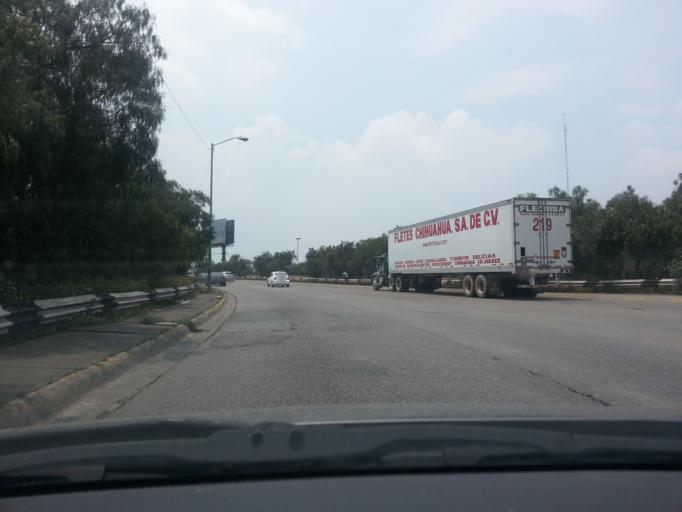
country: MX
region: Mexico
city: Cuautitlan
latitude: 19.6568
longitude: -99.1961
